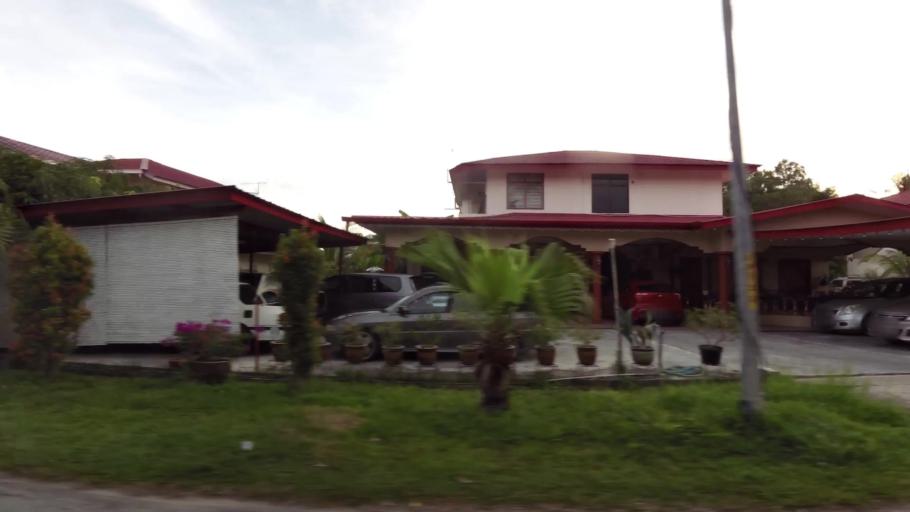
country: BN
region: Brunei and Muara
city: Bandar Seri Begawan
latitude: 4.9302
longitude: 114.8864
